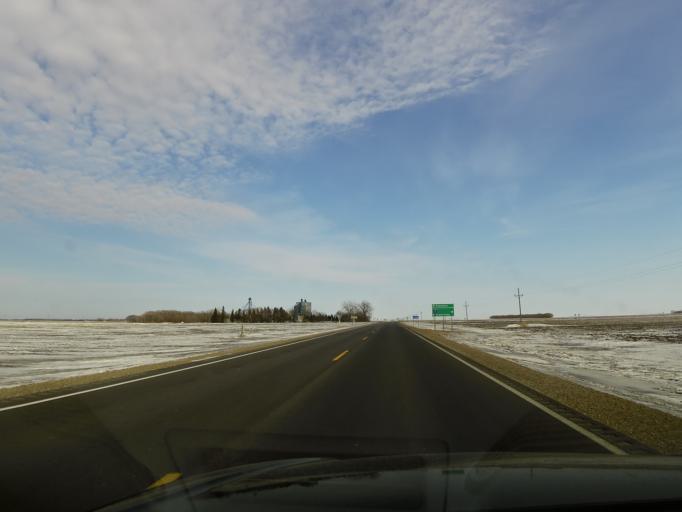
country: US
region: Minnesota
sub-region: Kittson County
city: Hallock
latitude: 48.5730
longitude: -97.1124
